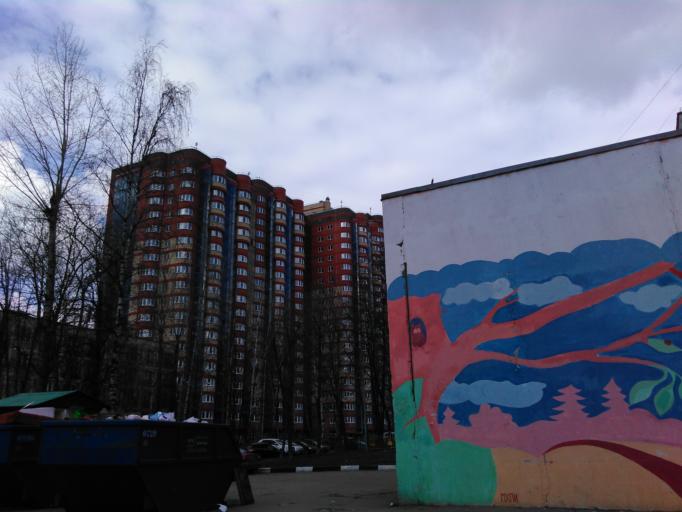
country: RU
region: Moscow
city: Troparevo
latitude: 55.6604
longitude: 37.5157
